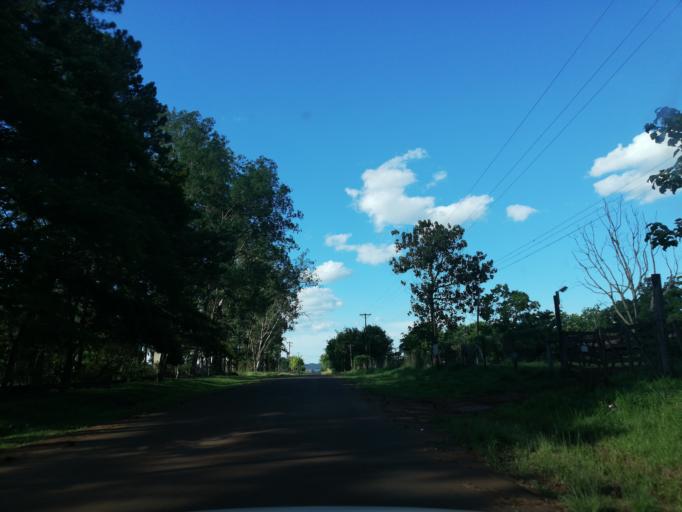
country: AR
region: Misiones
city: Garupa
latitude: -27.4633
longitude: -55.7973
